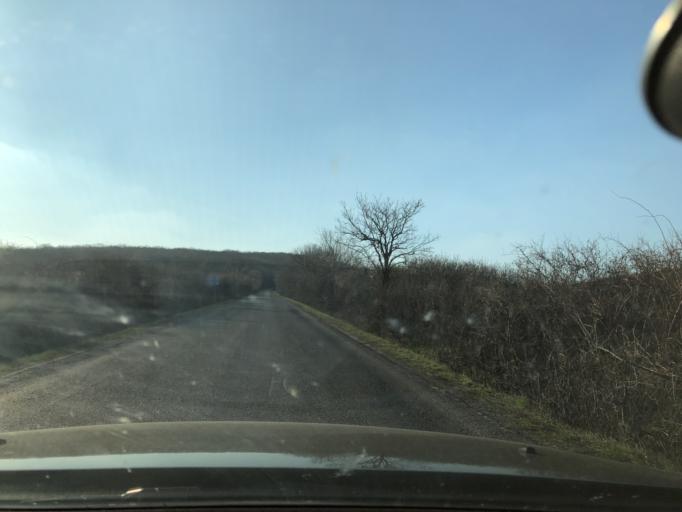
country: HU
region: Nograd
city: Paszto
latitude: 47.9139
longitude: 19.6461
